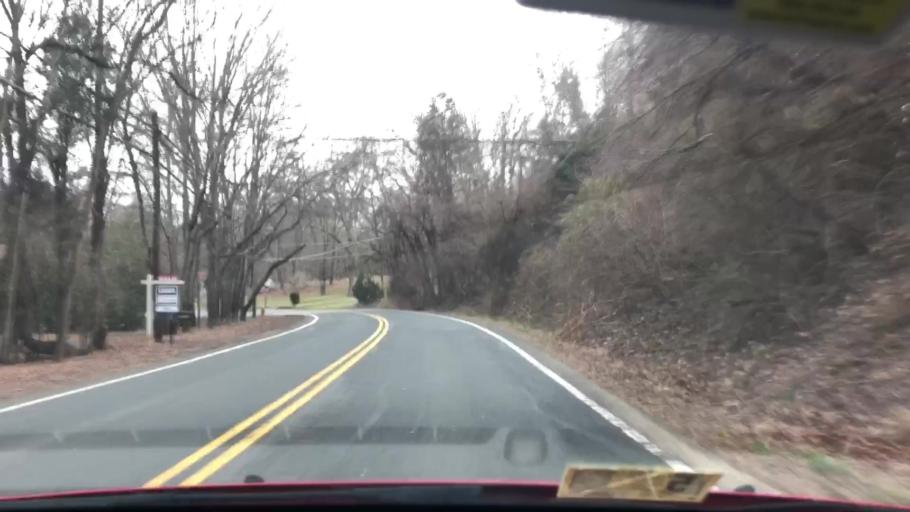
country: US
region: Virginia
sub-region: Fairfax County
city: Great Falls
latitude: 38.9718
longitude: -77.2953
